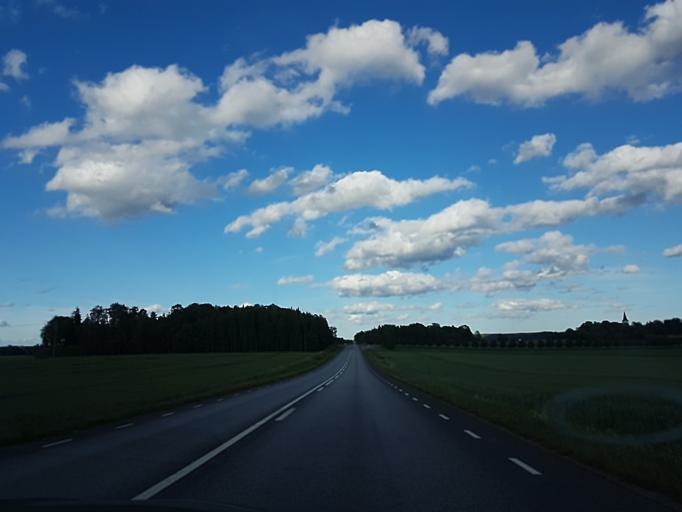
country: SE
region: Soedermanland
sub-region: Nykopings Kommun
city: Svalsta
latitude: 58.7411
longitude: 16.8235
